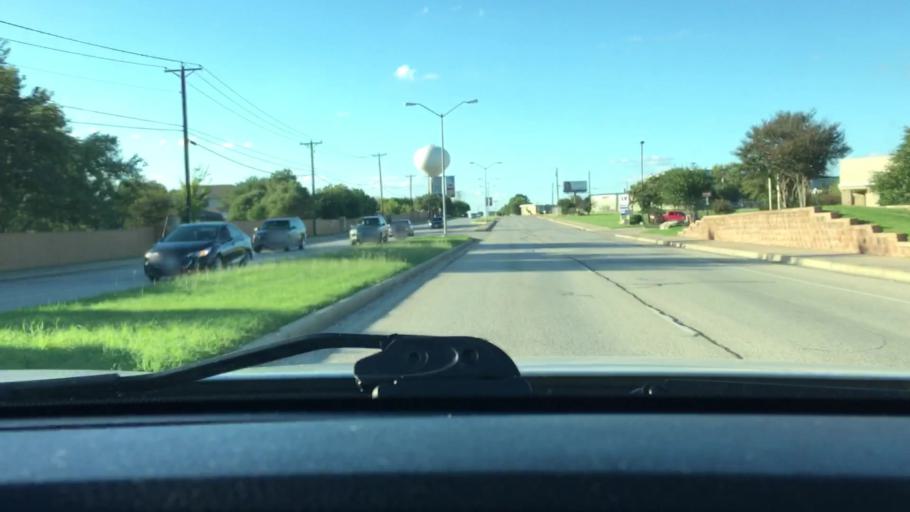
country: US
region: Texas
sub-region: Travis County
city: Windemere
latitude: 30.4751
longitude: -97.6422
